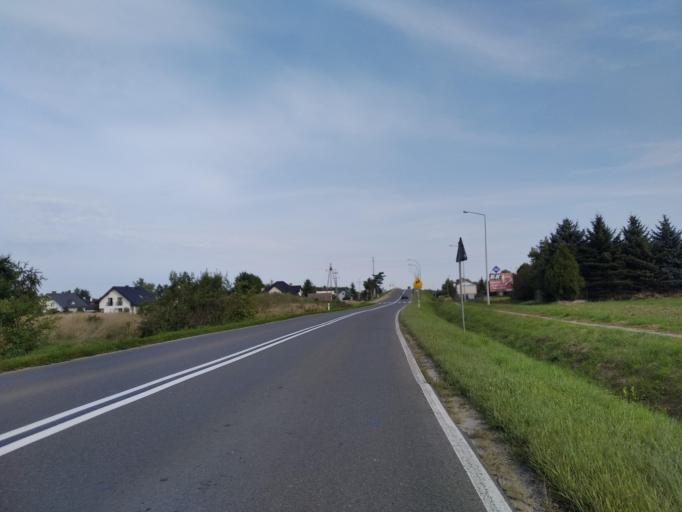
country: PL
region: Subcarpathian Voivodeship
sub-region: Powiat ropczycko-sedziszowski
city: Ostrow
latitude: 50.0754
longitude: 21.5839
